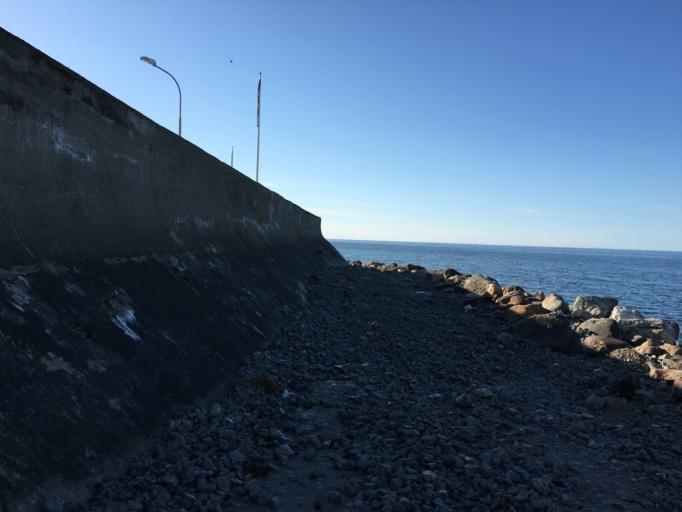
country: SE
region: Gotland
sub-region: Gotland
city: Visby
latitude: 57.6393
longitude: 18.2833
